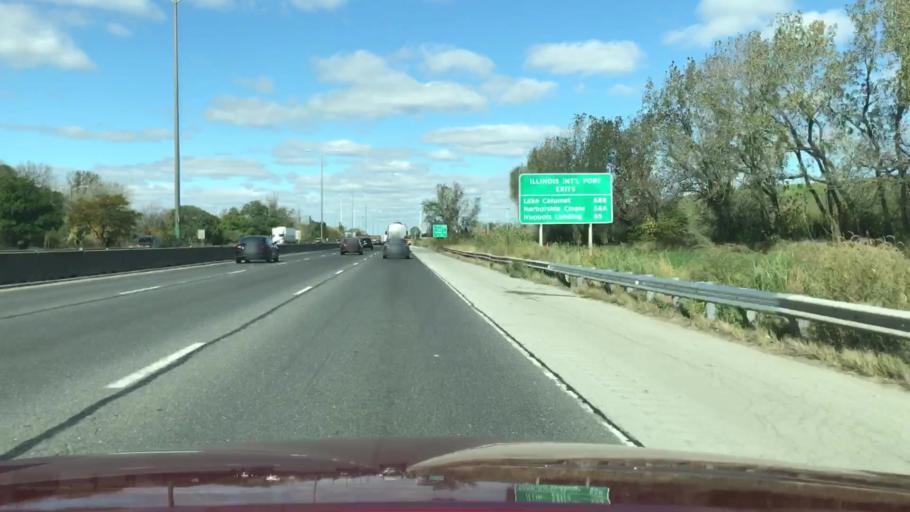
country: US
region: Illinois
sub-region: Cook County
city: Dolton
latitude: 41.6535
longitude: -87.5831
